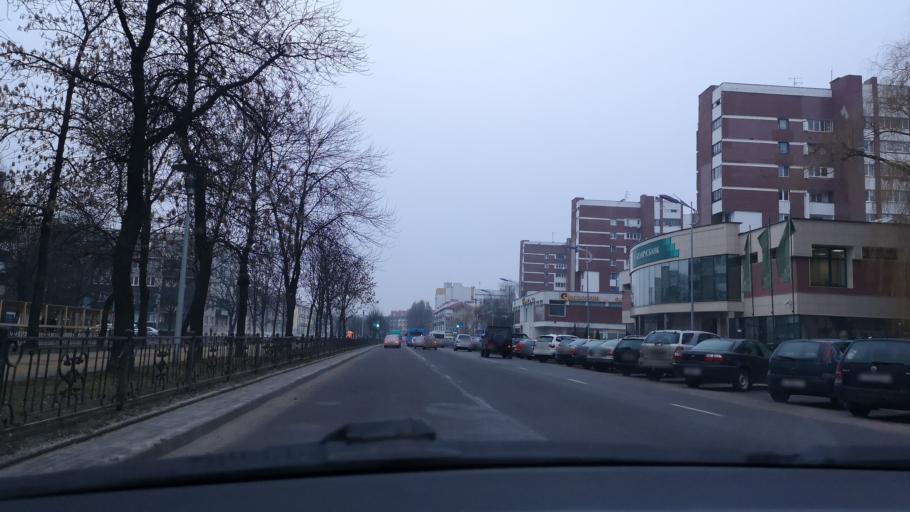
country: BY
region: Brest
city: Brest
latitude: 52.0907
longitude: 23.7014
